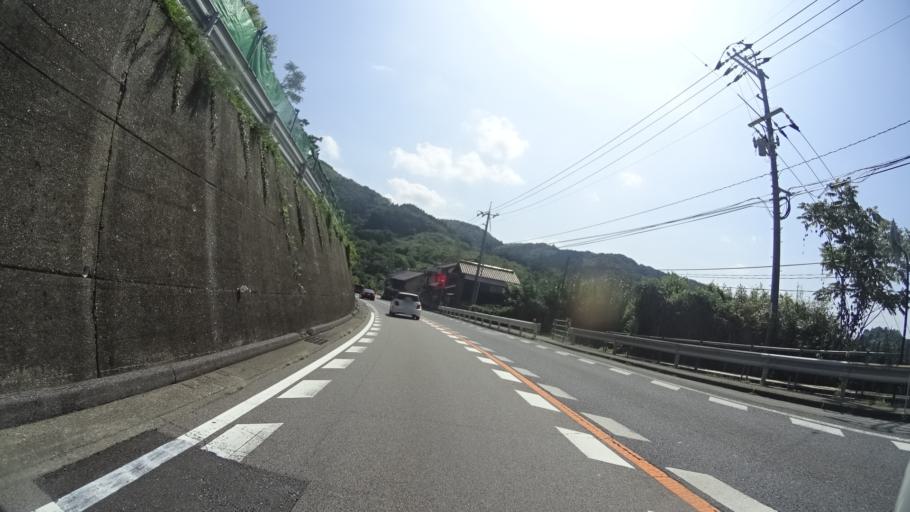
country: JP
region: Shimane
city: Masuda
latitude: 34.7450
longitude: 131.8740
